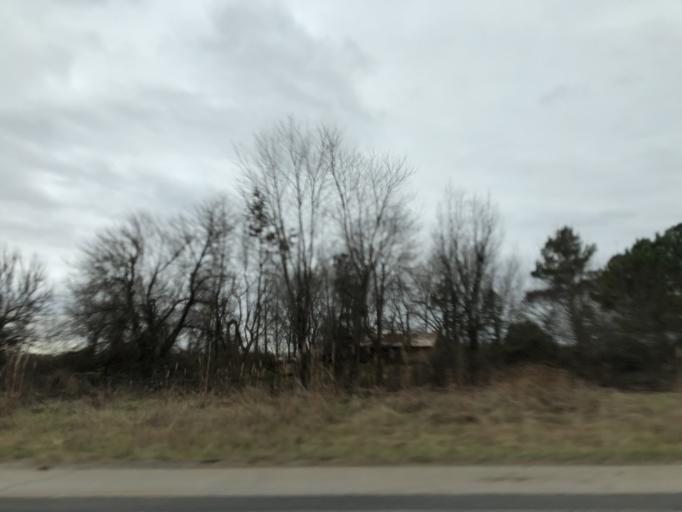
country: US
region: Illinois
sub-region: Massac County
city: Metropolis
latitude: 37.1896
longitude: -88.6849
